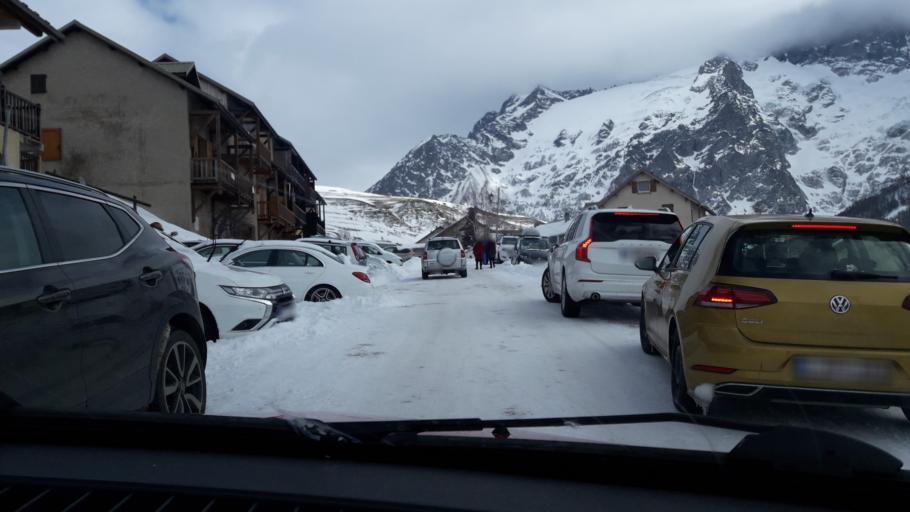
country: FR
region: Rhone-Alpes
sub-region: Departement de l'Isere
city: Mont-de-Lans
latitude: 45.0551
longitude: 6.2848
